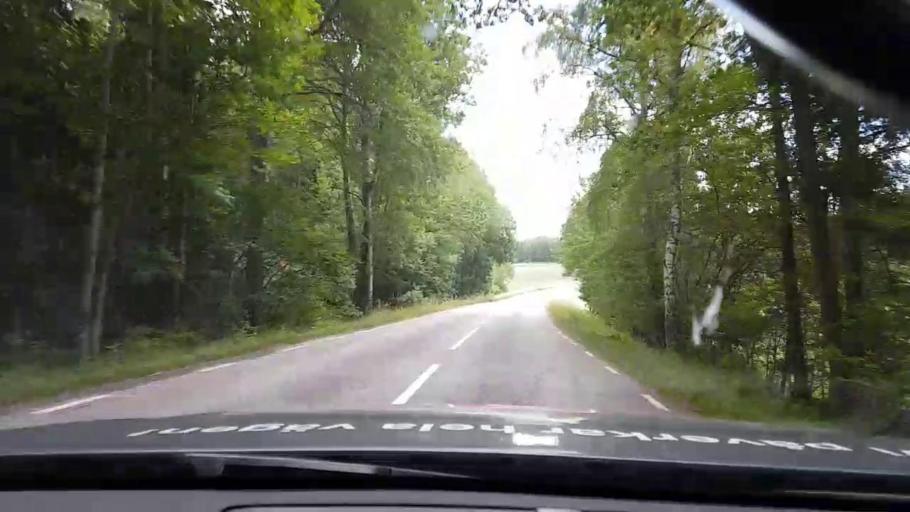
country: SE
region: Kalmar
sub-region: Vasterviks Kommun
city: Overum
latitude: 58.0650
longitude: 16.3985
